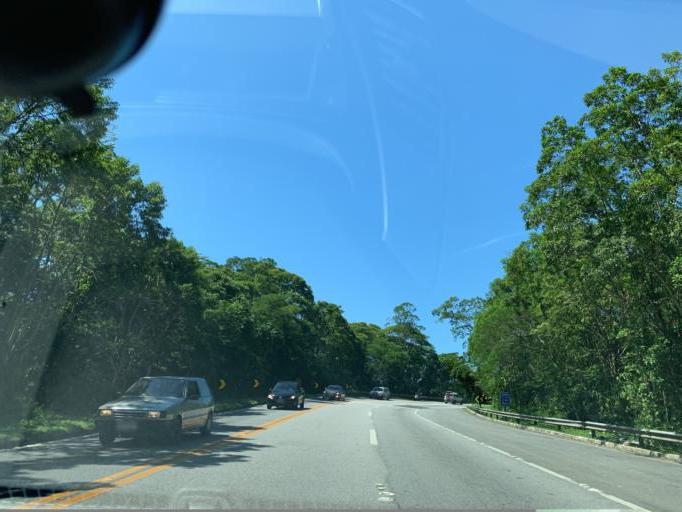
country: BR
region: Sao Paulo
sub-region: Bertioga
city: Bertioga
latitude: -23.7499
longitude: -46.0406
